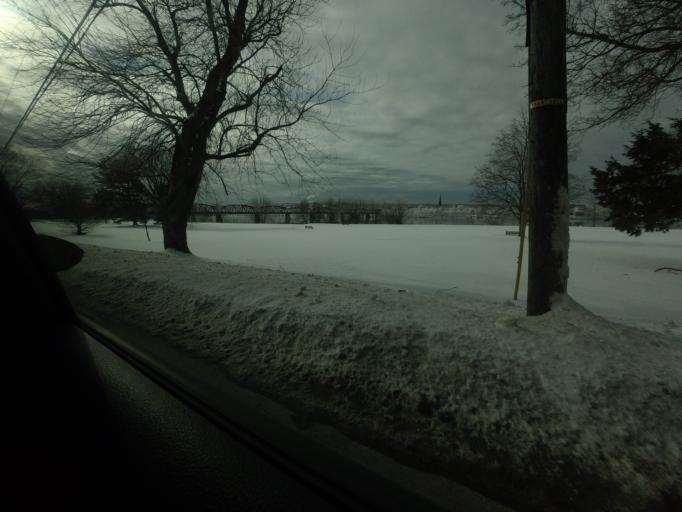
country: CA
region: New Brunswick
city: Fredericton
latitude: 45.9610
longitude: -66.6249
